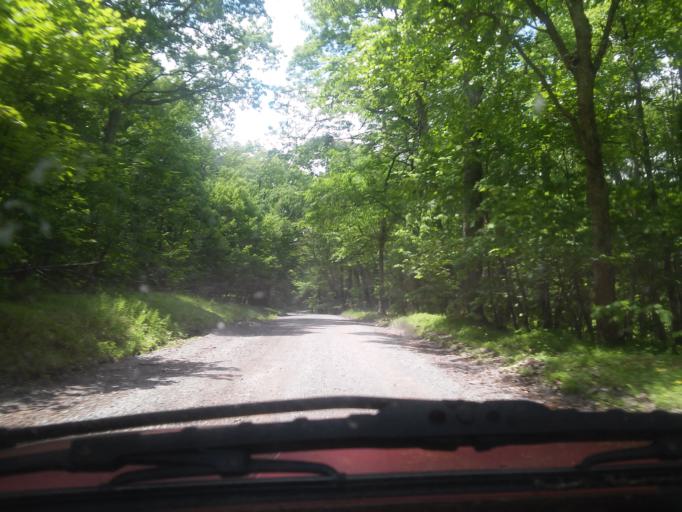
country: US
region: Virginia
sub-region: Giles County
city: Pembroke
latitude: 37.3710
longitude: -80.5280
